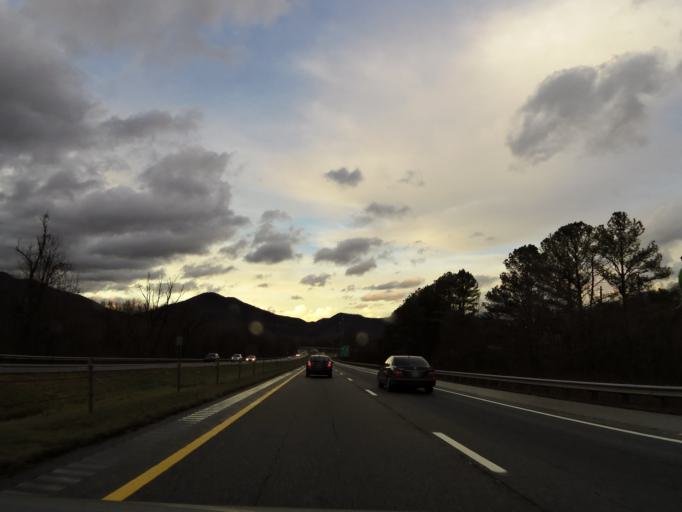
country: US
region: Tennessee
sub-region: Campbell County
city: Caryville
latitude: 36.2923
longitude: -84.2148
